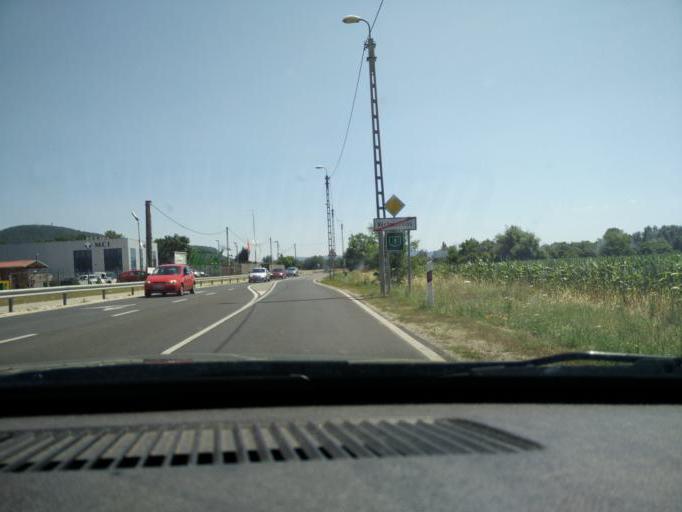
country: HU
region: Komarom-Esztergom
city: Vertesszolos
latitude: 47.6123
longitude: 18.3828
